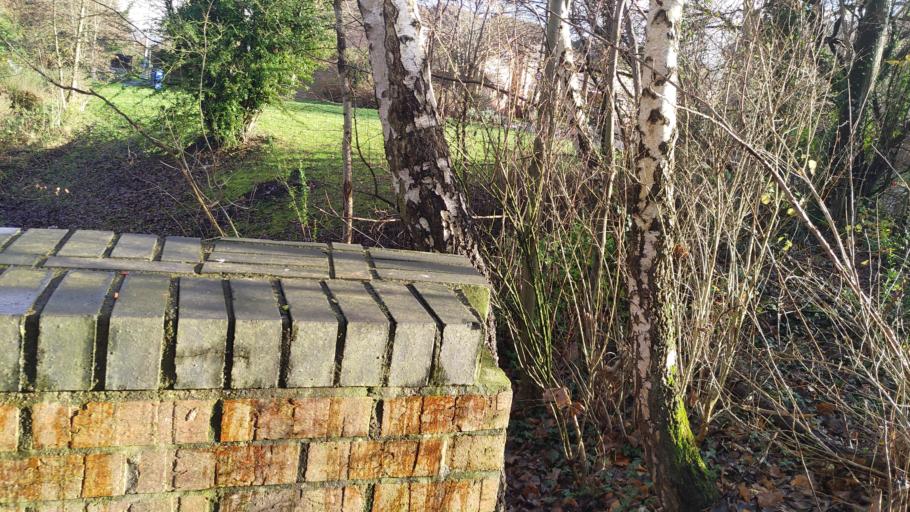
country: GB
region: England
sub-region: Lancashire
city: Leyland
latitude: 53.6969
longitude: -2.6964
